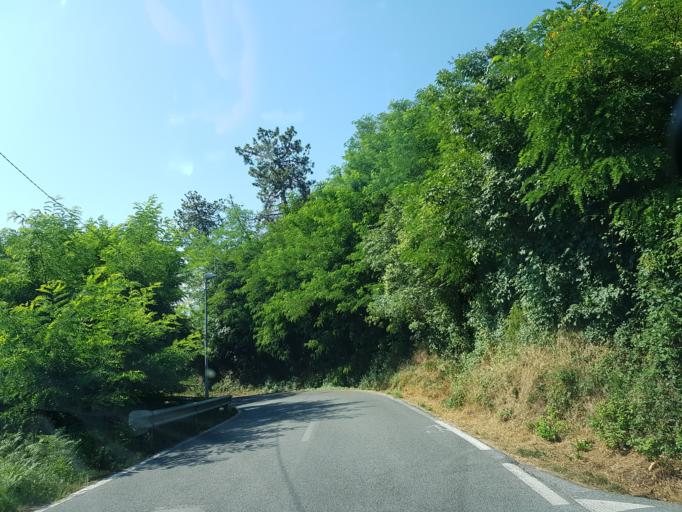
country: IT
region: Liguria
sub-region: Provincia di Genova
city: Manesseno
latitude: 44.4883
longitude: 8.9110
